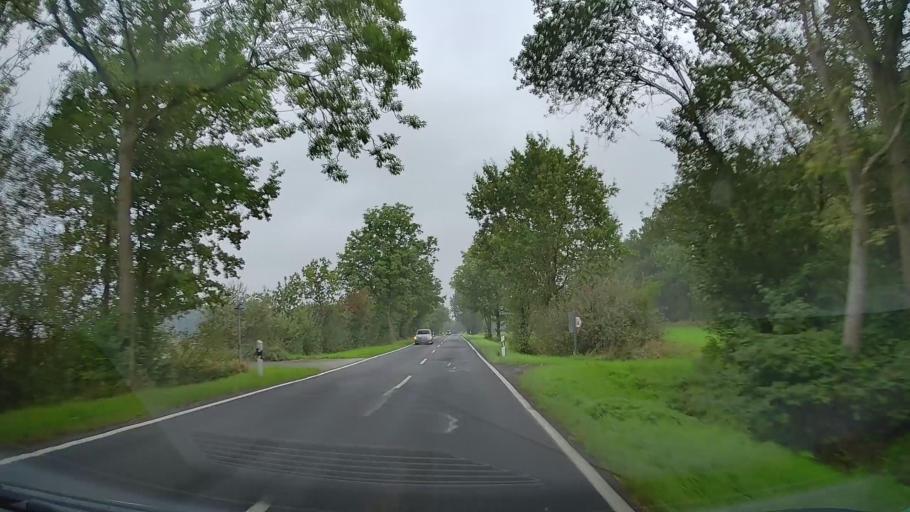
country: DE
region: Mecklenburg-Vorpommern
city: Neubukow
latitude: 54.0819
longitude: 11.6315
